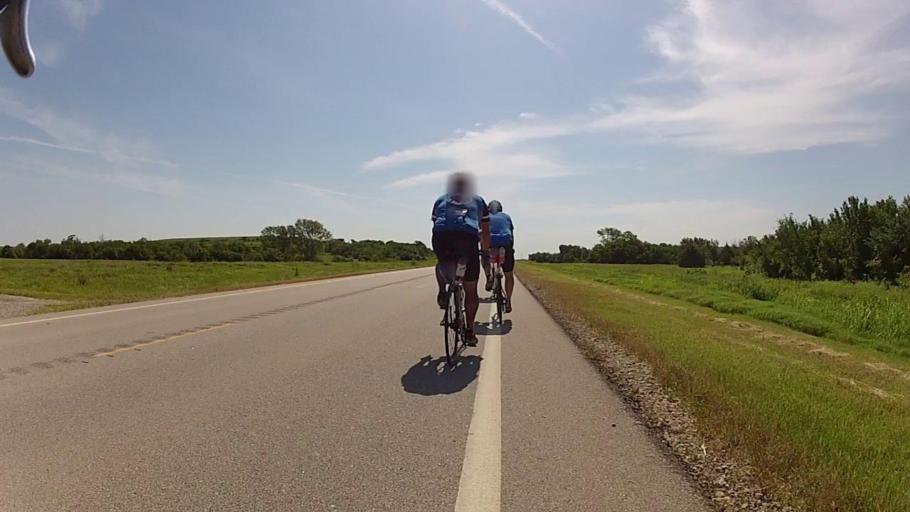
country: US
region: Kansas
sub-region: Chautauqua County
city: Sedan
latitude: 37.1072
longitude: -96.5764
